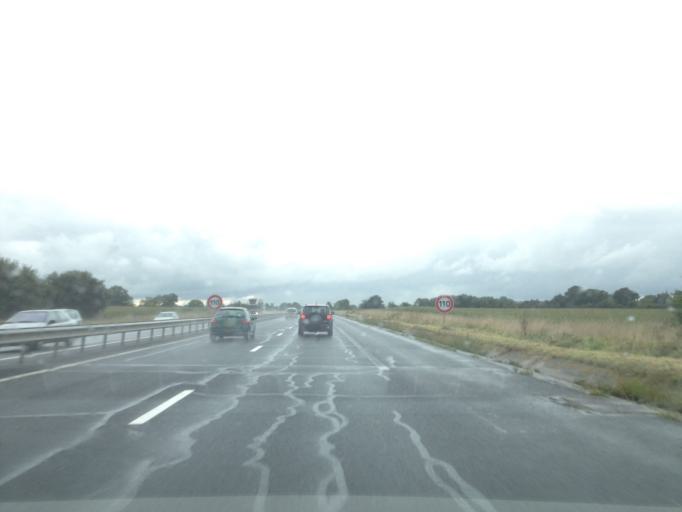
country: FR
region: Lower Normandy
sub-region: Departement du Calvados
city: Port-en-Bessin-Huppain
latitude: 49.2896
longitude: -0.7656
